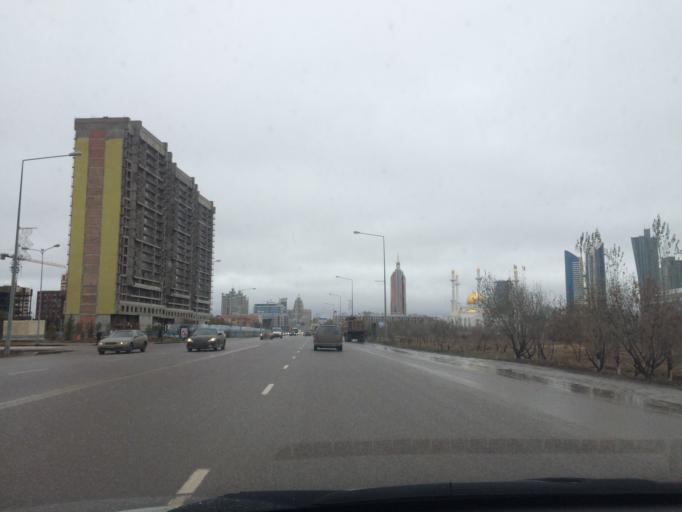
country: KZ
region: Astana Qalasy
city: Astana
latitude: 51.1217
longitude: 71.4124
